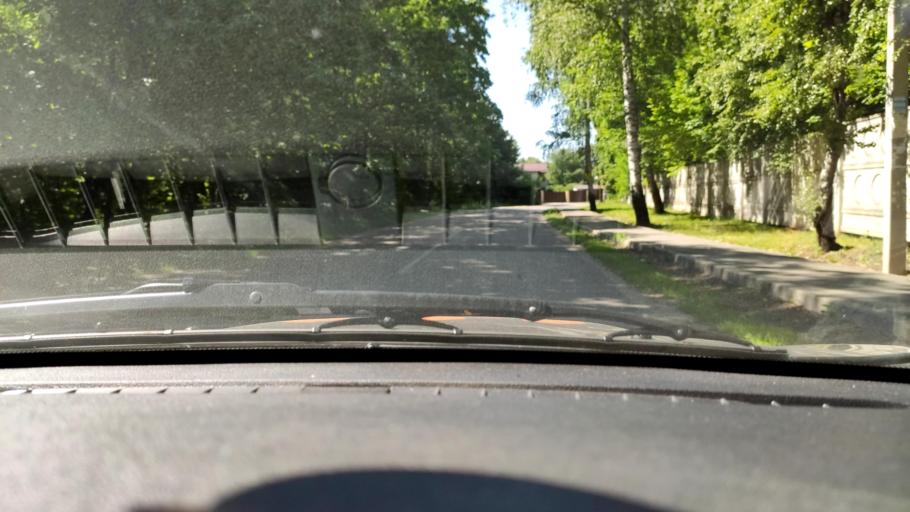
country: RU
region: Voronezj
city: Ramon'
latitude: 51.8233
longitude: 39.2621
